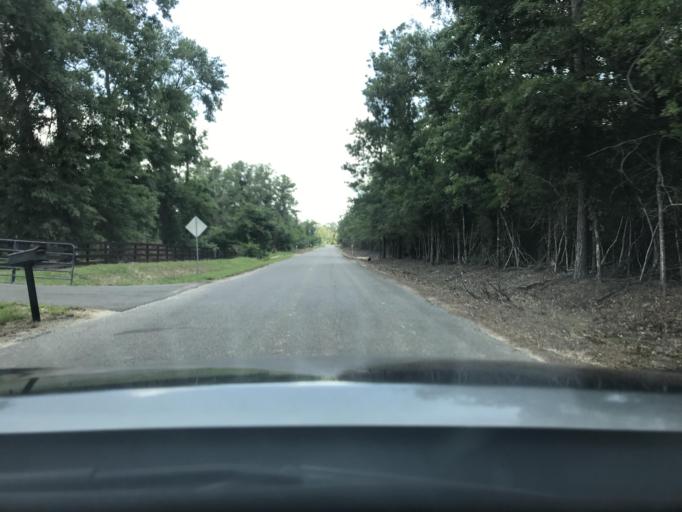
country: US
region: Louisiana
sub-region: Calcasieu Parish
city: Moss Bluff
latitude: 30.3347
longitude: -93.1308
